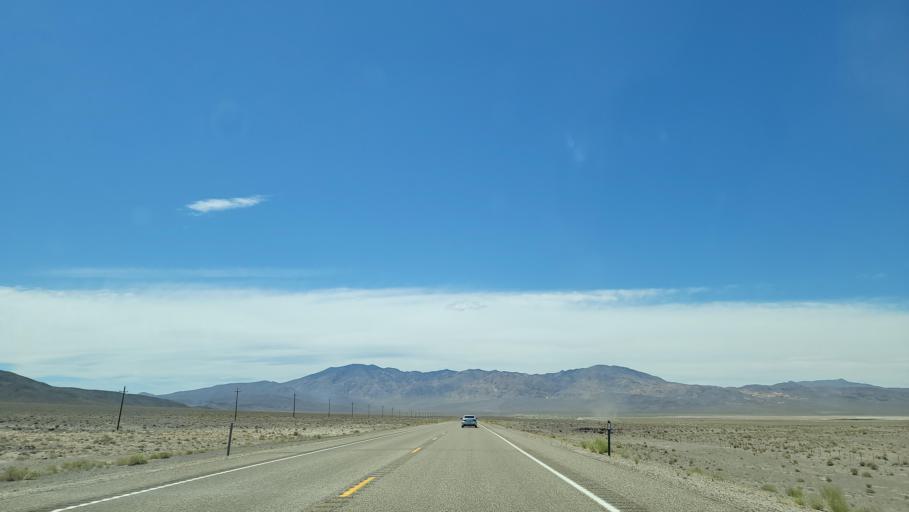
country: US
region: Nevada
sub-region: Mineral County
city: Hawthorne
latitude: 38.2386
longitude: -118.0348
